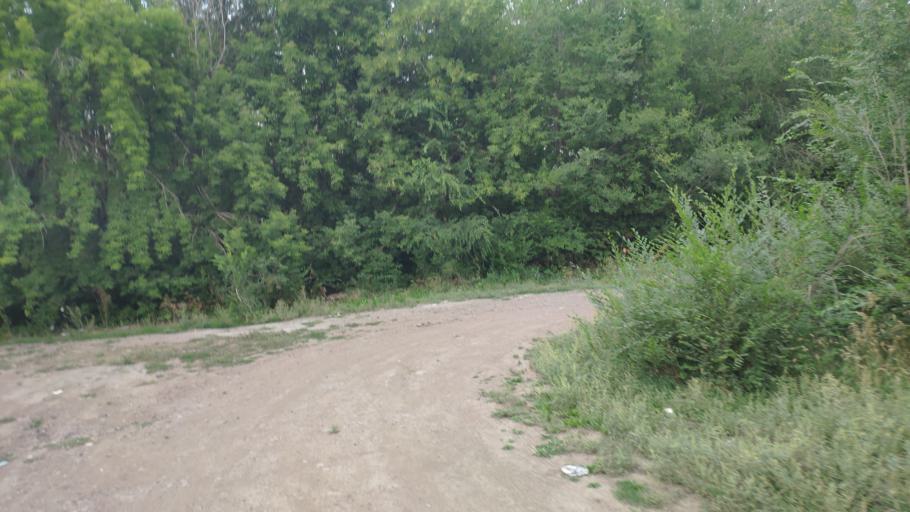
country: RU
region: Chelyabinsk
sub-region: Gorod Magnitogorsk
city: Magnitogorsk
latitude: 53.4145
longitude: 59.0020
